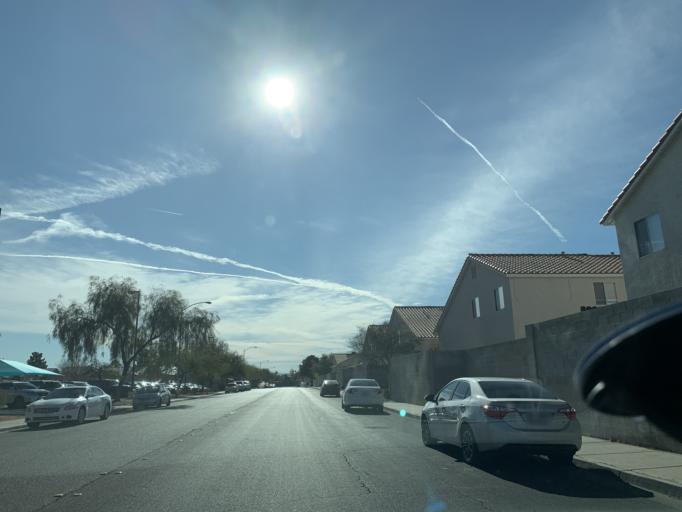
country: US
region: Nevada
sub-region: Clark County
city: Spring Valley
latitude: 36.0960
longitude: -115.2208
